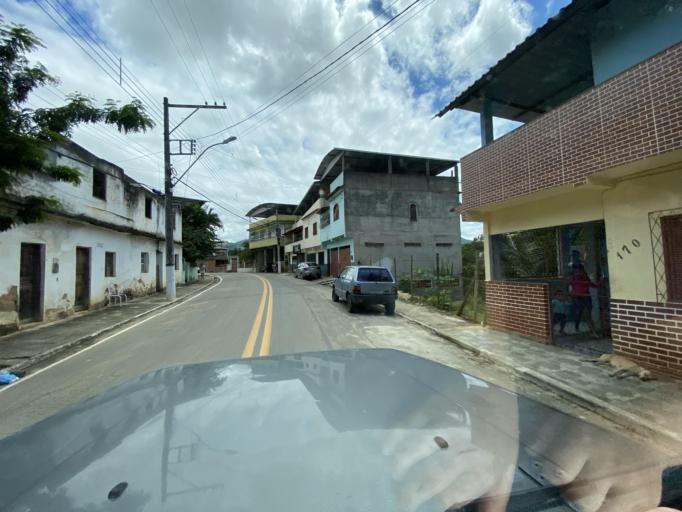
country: BR
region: Espirito Santo
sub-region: Jeronimo Monteiro
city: Jeronimo Monteiro
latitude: -20.7926
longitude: -41.4003
